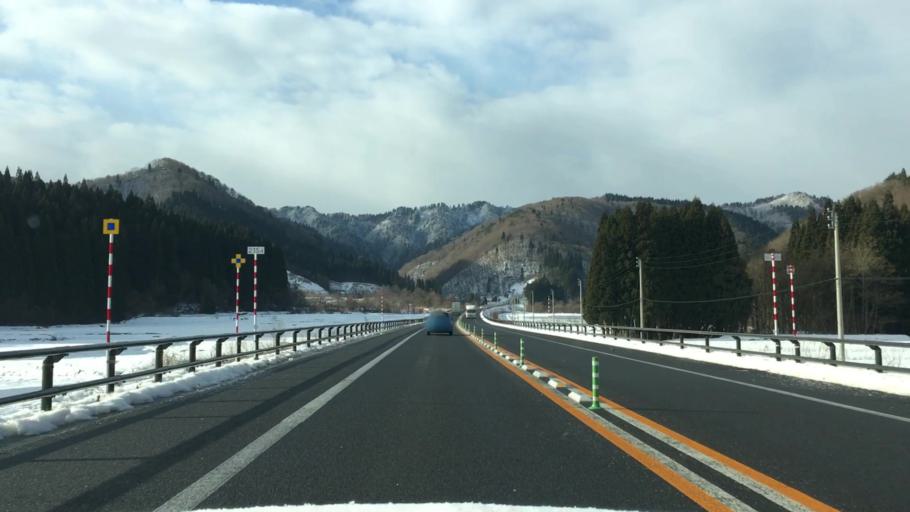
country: JP
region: Akita
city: Odate
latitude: 40.2349
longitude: 140.4982
